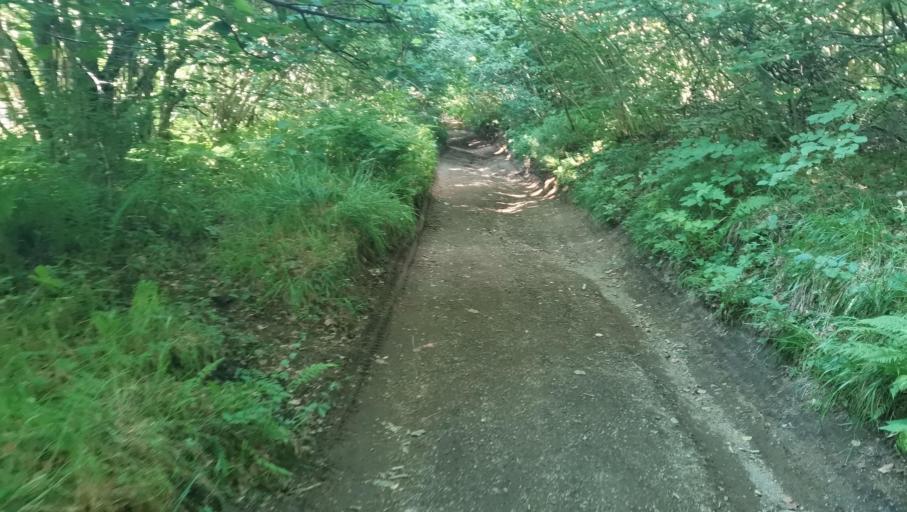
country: FR
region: Auvergne
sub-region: Departement du Puy-de-Dome
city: Orcines
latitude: 45.7989
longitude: 2.9644
